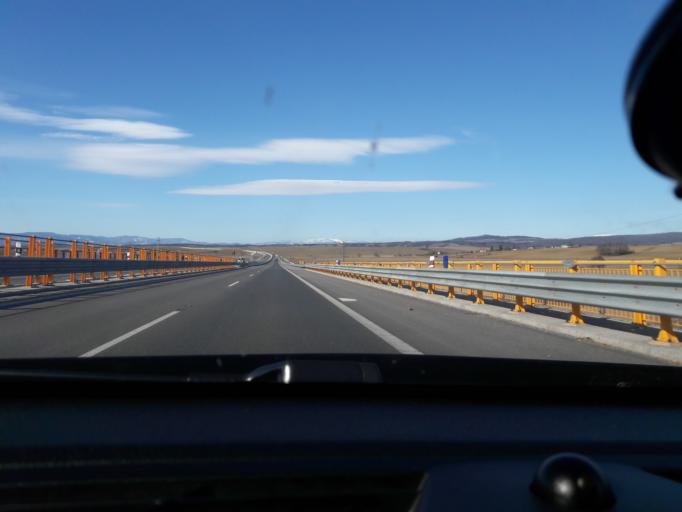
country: SK
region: Banskobystricky
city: Detva
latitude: 48.5540
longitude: 19.3214
